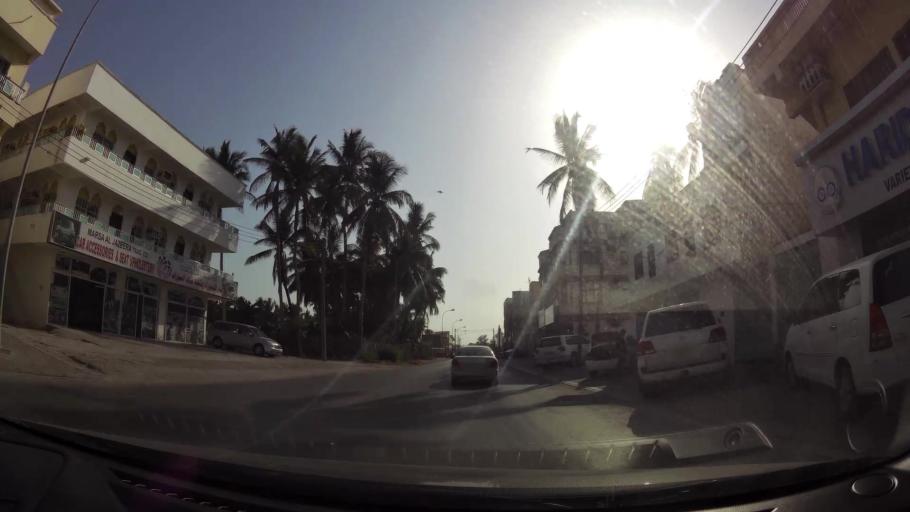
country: OM
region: Zufar
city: Salalah
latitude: 17.0094
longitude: 54.0940
